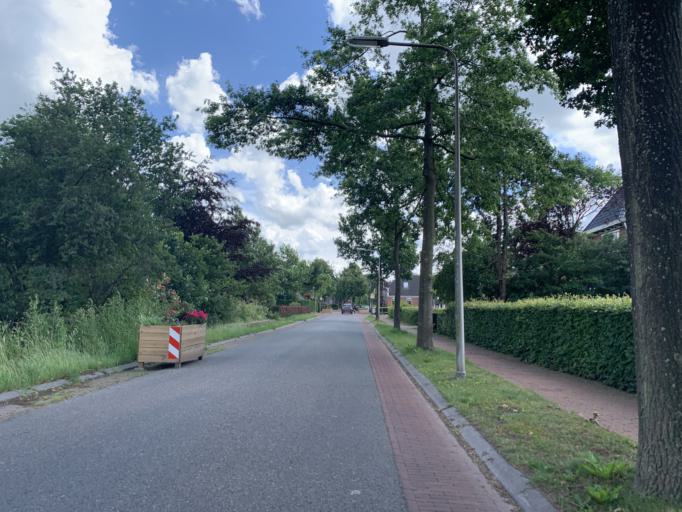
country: NL
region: Groningen
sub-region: Gemeente Haren
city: Haren
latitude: 53.1591
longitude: 6.6395
